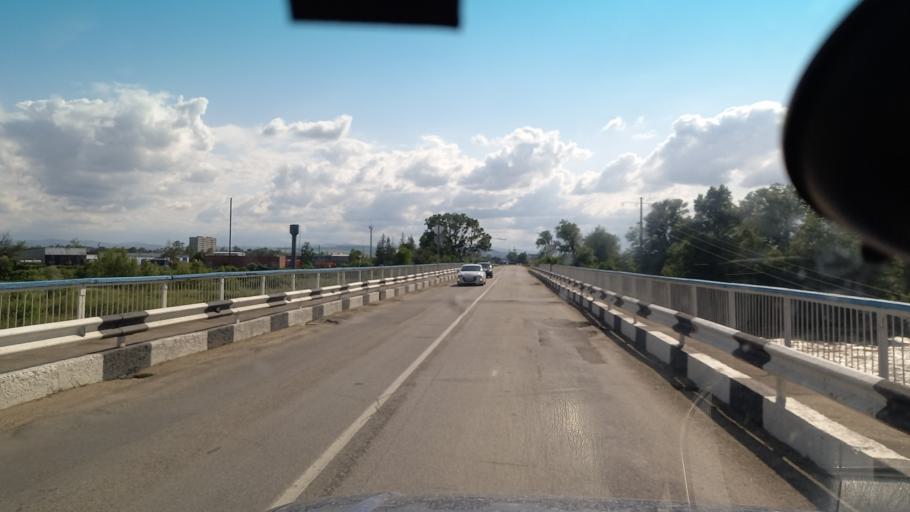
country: RU
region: Krasnodarskiy
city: Mostovskoy
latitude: 44.3999
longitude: 40.8209
